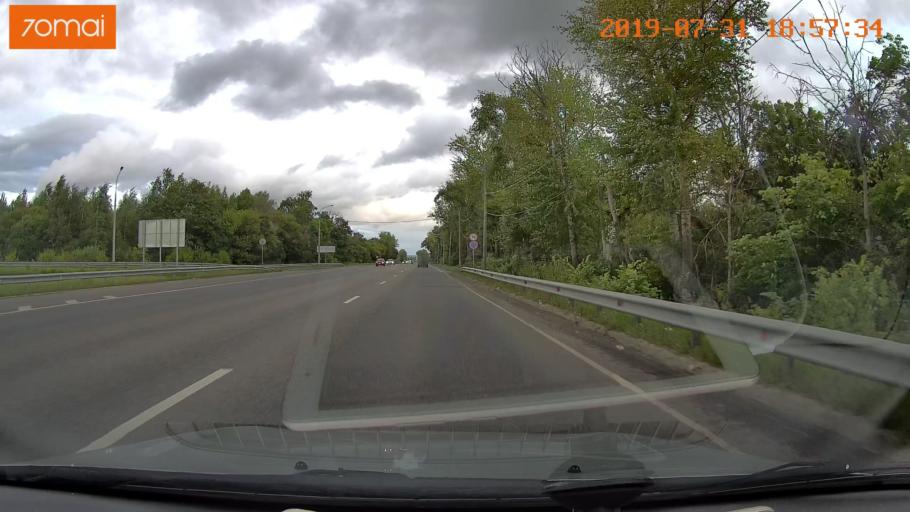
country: RU
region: Moskovskaya
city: Raduzhnyy
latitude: 55.1531
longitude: 38.6939
